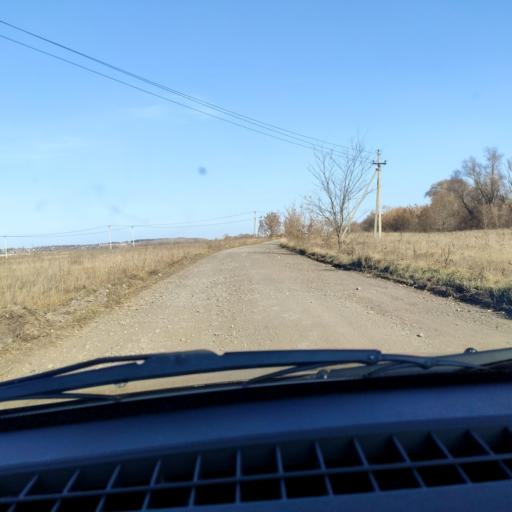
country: RU
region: Bashkortostan
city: Avdon
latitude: 54.4959
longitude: 55.8635
